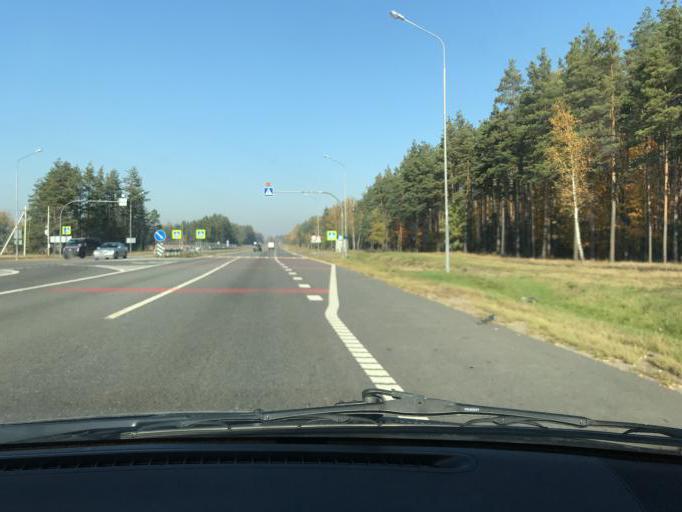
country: BY
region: Minsk
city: Slutsk
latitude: 53.3245
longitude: 27.5331
